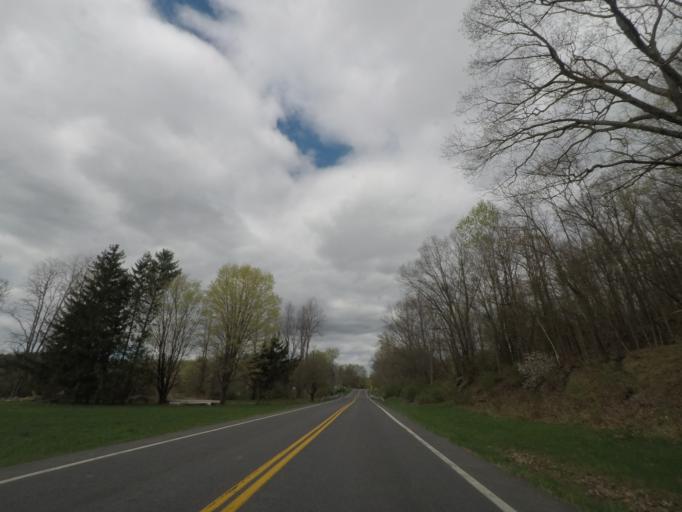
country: US
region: New York
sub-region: Columbia County
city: Chatham
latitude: 42.3158
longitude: -73.6261
